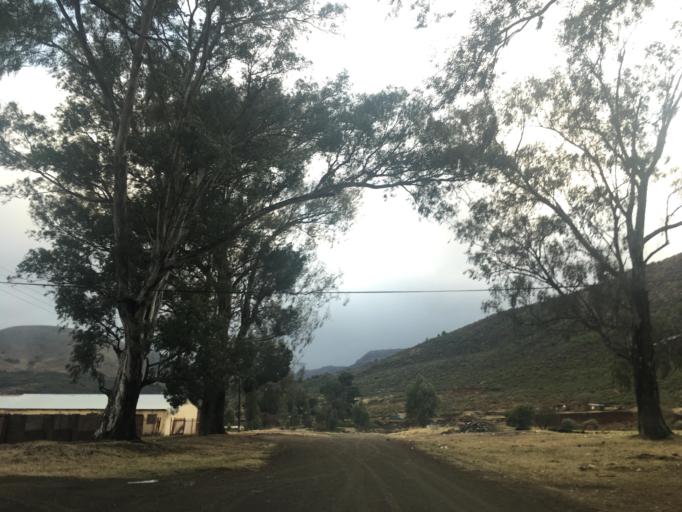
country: ZA
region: Eastern Cape
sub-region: Chris Hani District Municipality
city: Cala
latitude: -31.5204
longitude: 27.7014
